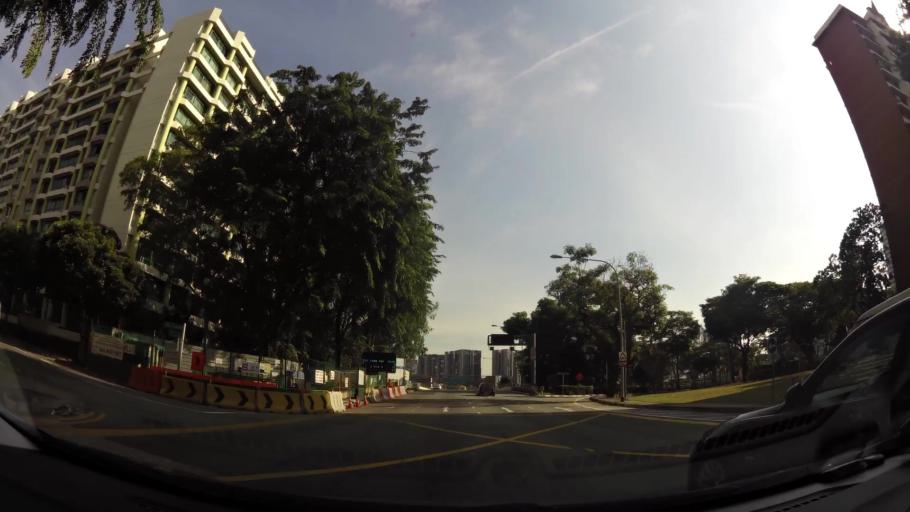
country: SG
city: Singapore
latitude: 1.3248
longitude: 103.8657
